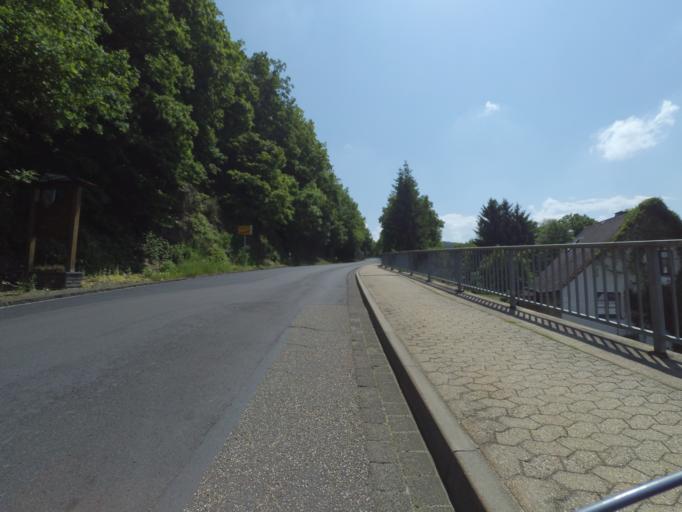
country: DE
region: Rheinland-Pfalz
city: Urmersbach
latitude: 50.2563
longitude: 7.1322
